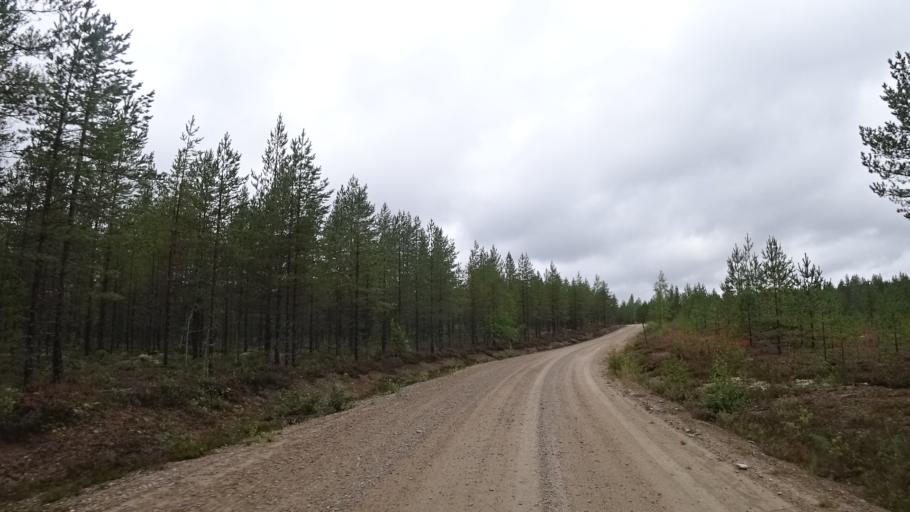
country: FI
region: North Karelia
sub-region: Pielisen Karjala
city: Lieksa
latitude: 63.5134
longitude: 30.1281
